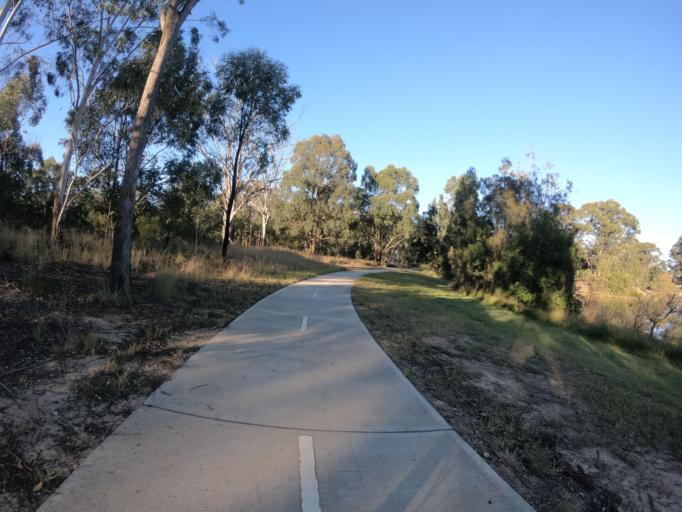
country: AU
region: New South Wales
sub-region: Hawkesbury
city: South Windsor
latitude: -33.6347
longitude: 150.8113
